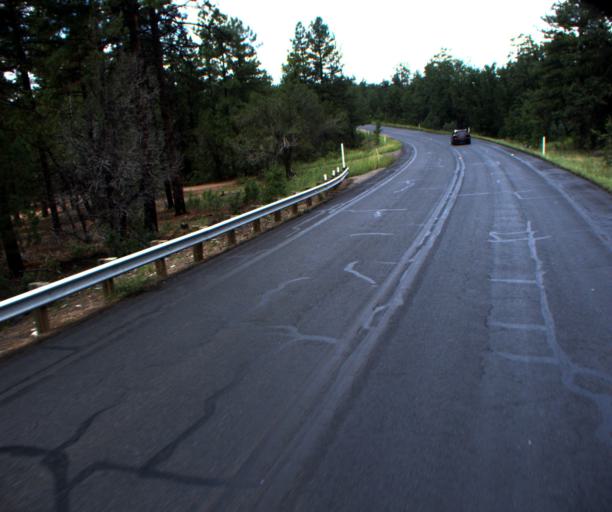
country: US
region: Arizona
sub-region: Gila County
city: Pine
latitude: 34.5195
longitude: -111.5069
